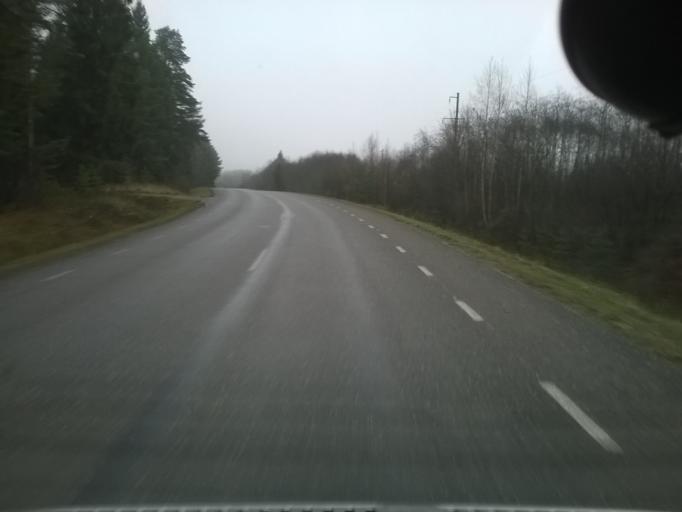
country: EE
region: Raplamaa
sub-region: Kohila vald
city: Kohila
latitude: 59.1435
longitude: 24.6010
